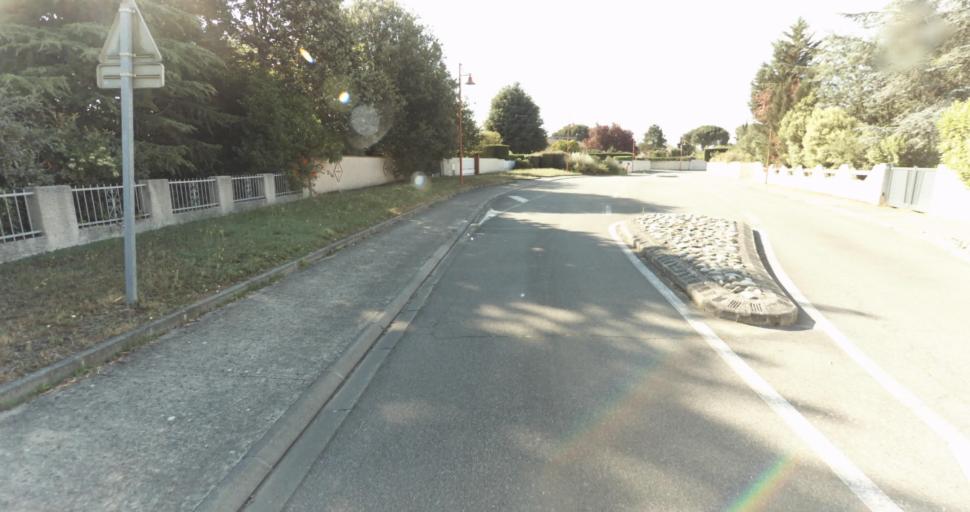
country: FR
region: Midi-Pyrenees
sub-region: Departement de la Haute-Garonne
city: Fontenilles
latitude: 43.5663
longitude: 1.2056
